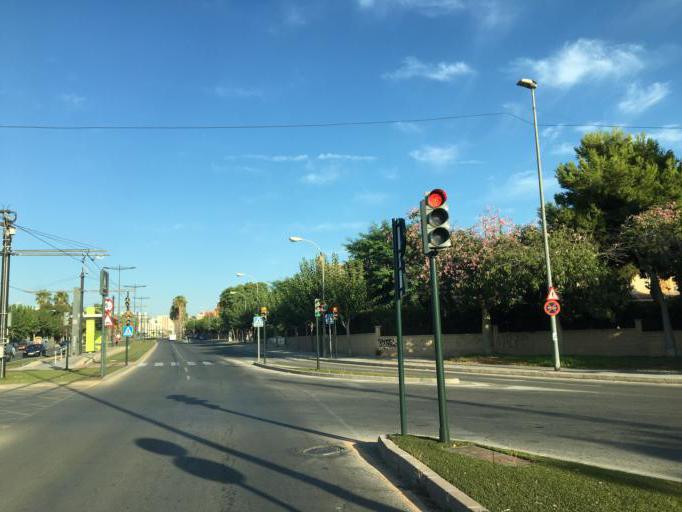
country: ES
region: Murcia
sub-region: Murcia
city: Murcia
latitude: 38.0126
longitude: -1.1514
